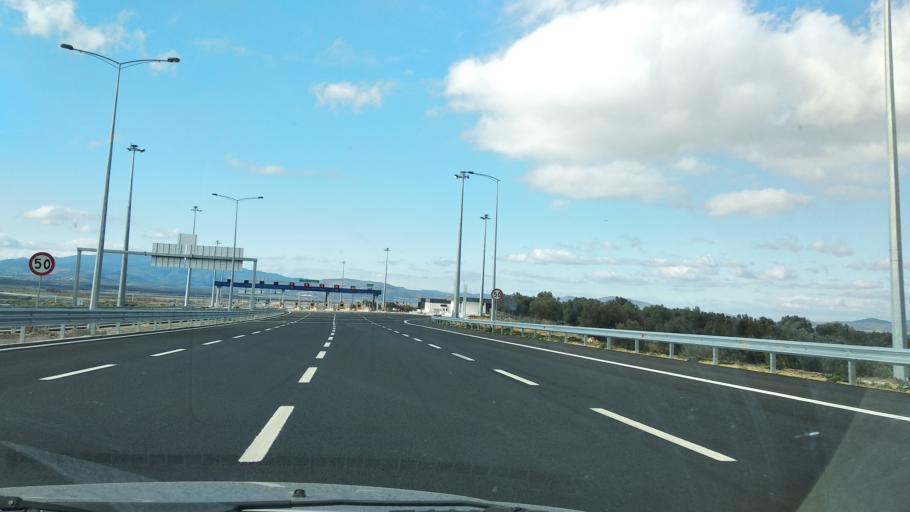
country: TR
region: Izmir
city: Zeytindag
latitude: 38.9729
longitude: 27.0564
